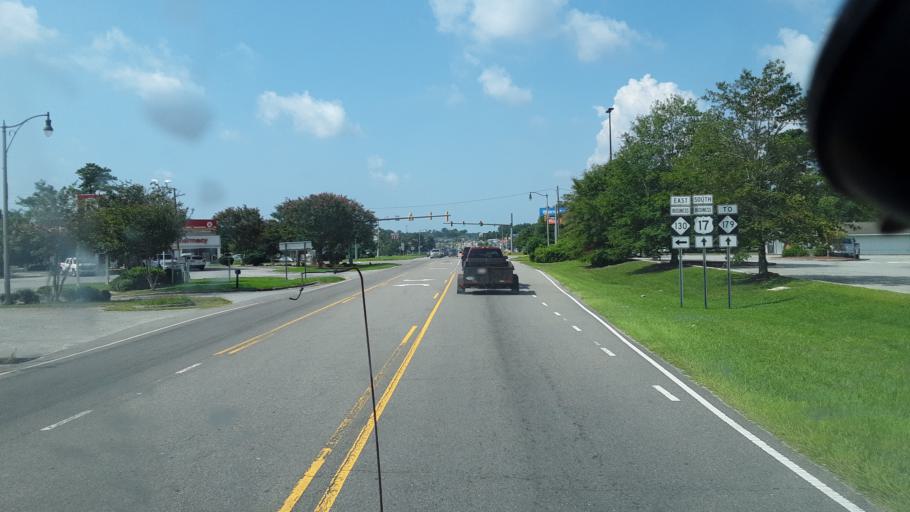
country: US
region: North Carolina
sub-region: Brunswick County
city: Shallotte
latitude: 33.9823
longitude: -78.3723
